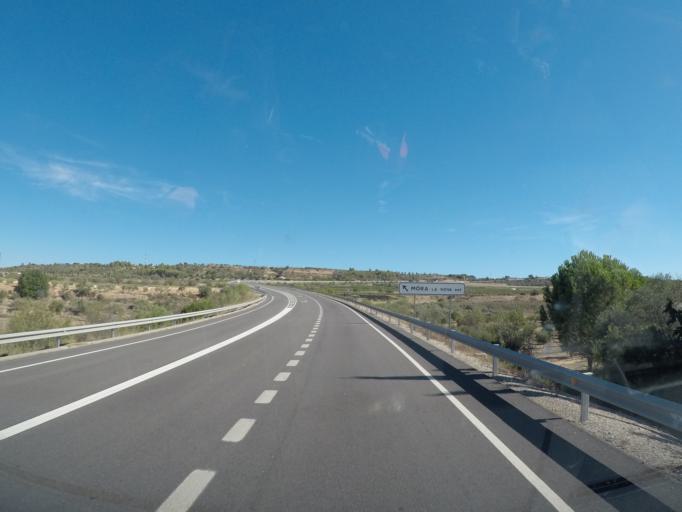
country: ES
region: Catalonia
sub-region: Provincia de Tarragona
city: Garcia
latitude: 41.0992
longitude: 0.6598
